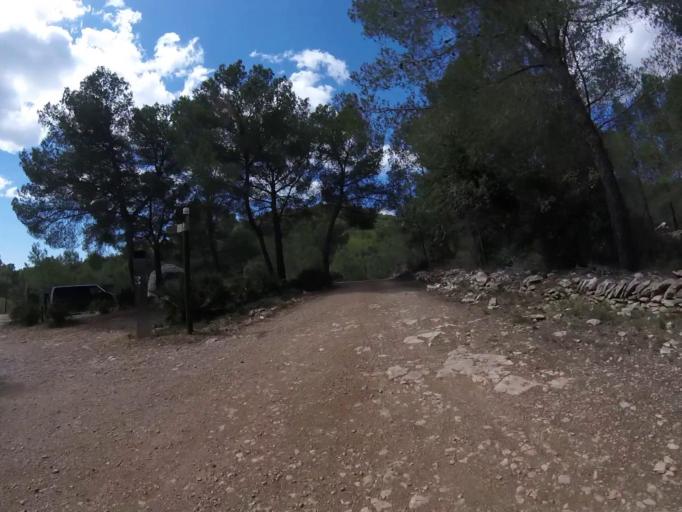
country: ES
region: Valencia
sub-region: Provincia de Castello
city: Santa Magdalena de Pulpis
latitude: 40.3120
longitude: 0.3275
